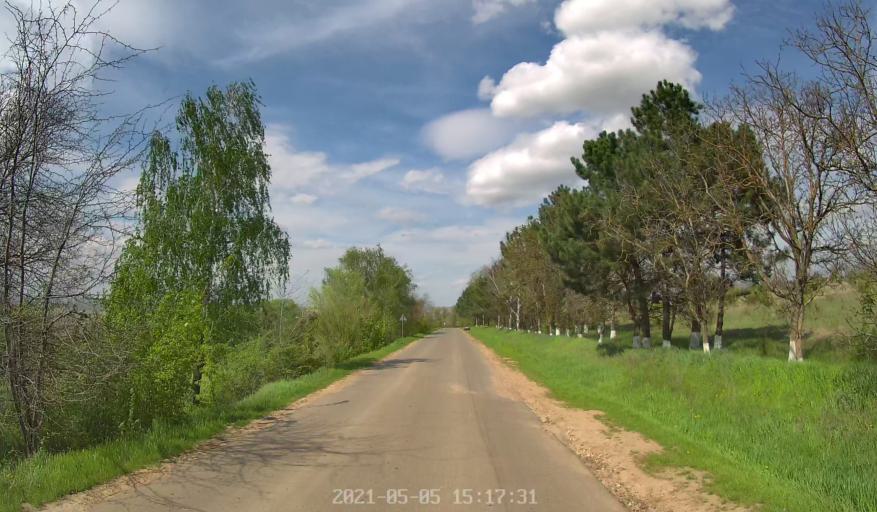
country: MD
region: Criuleni
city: Criuleni
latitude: 47.1124
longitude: 29.1940
